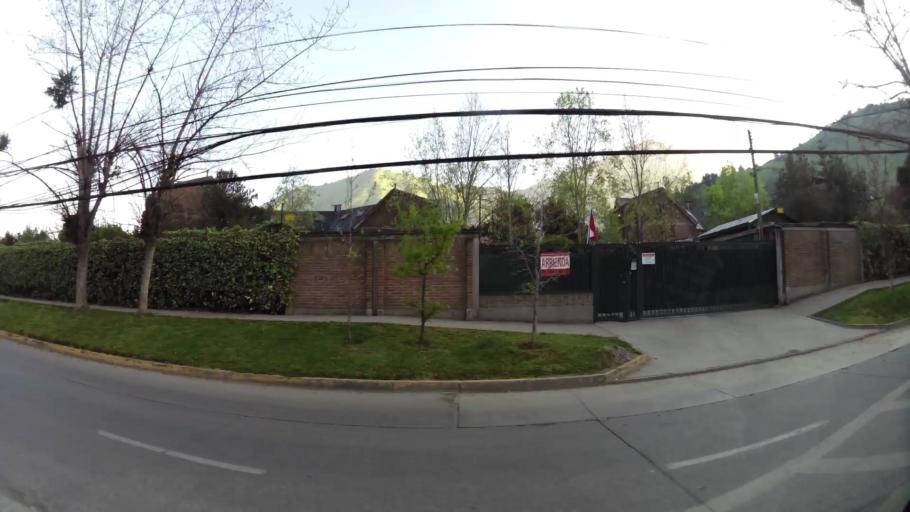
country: CL
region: Santiago Metropolitan
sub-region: Provincia de Santiago
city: Santiago
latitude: -33.3841
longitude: -70.6140
